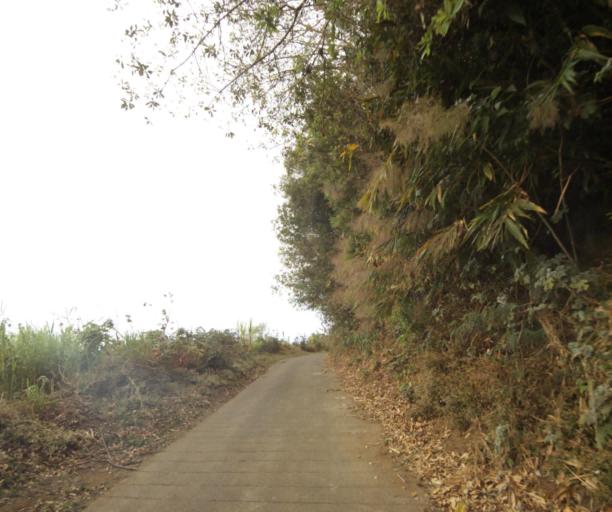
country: RE
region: Reunion
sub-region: Reunion
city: Saint-Paul
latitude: -21.0225
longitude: 55.3233
